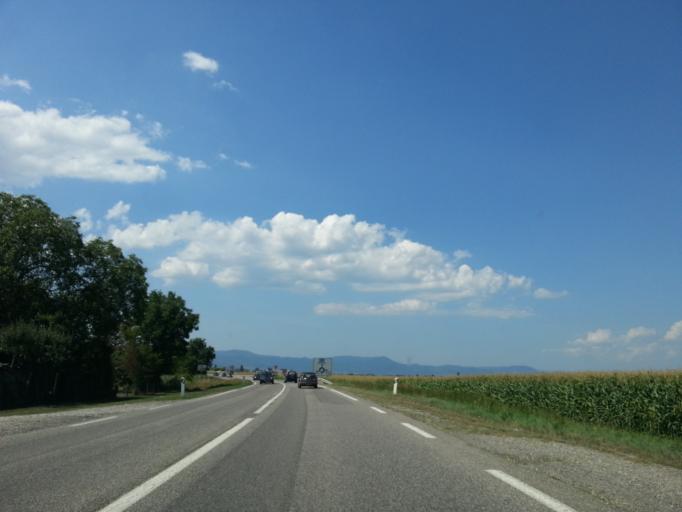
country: FR
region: Alsace
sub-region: Departement du Haut-Rhin
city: Andolsheim
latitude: 48.0643
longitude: 7.4205
